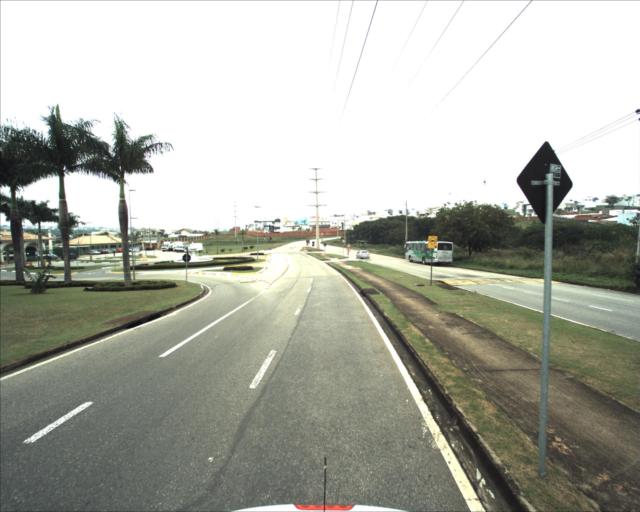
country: BR
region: Sao Paulo
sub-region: Sorocaba
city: Sorocaba
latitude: -23.4453
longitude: -47.4538
